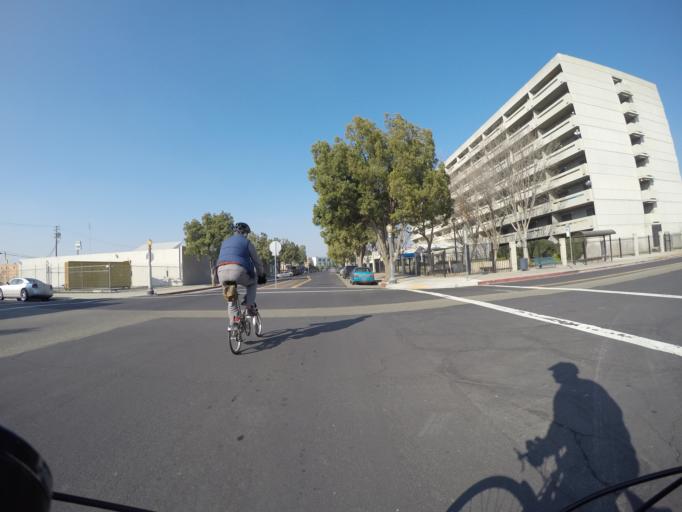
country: US
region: California
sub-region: Fresno County
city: Fresno
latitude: 36.7418
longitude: -119.7987
